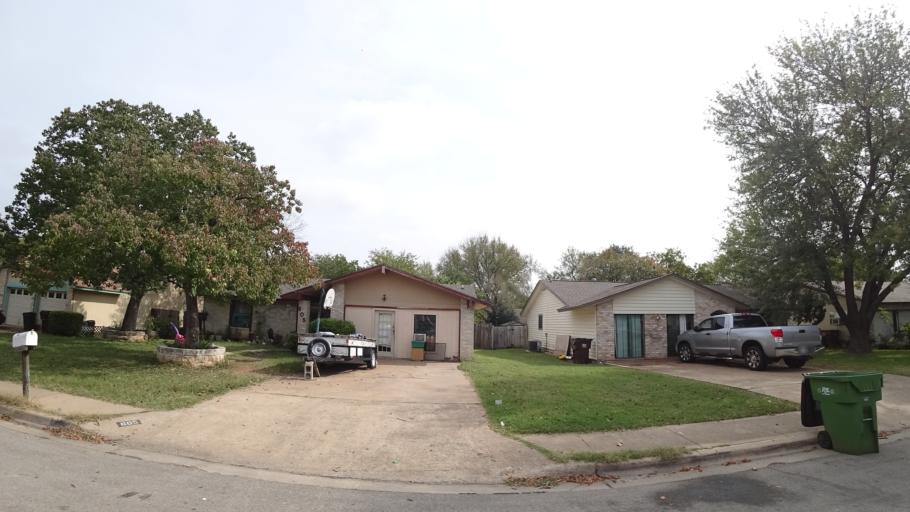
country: US
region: Texas
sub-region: Williamson County
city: Round Rock
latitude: 30.4947
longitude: -97.6849
